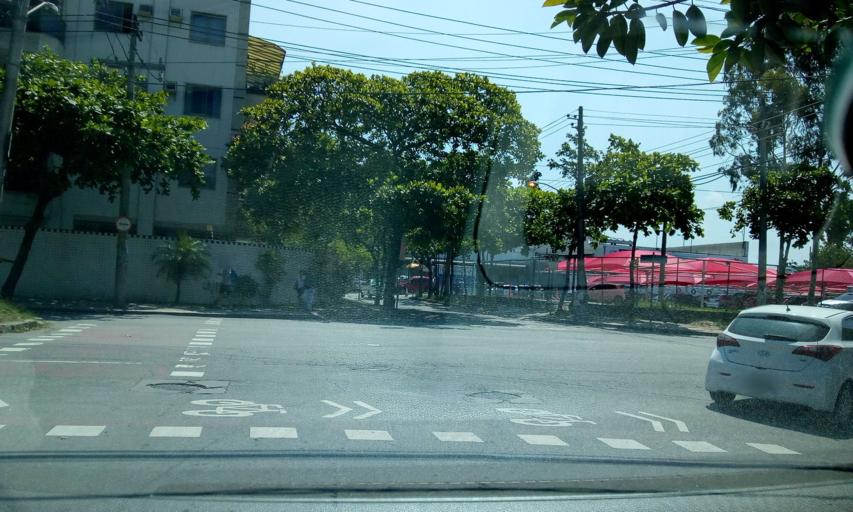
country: BR
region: Rio de Janeiro
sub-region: Nilopolis
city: Nilopolis
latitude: -23.0141
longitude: -43.4611
